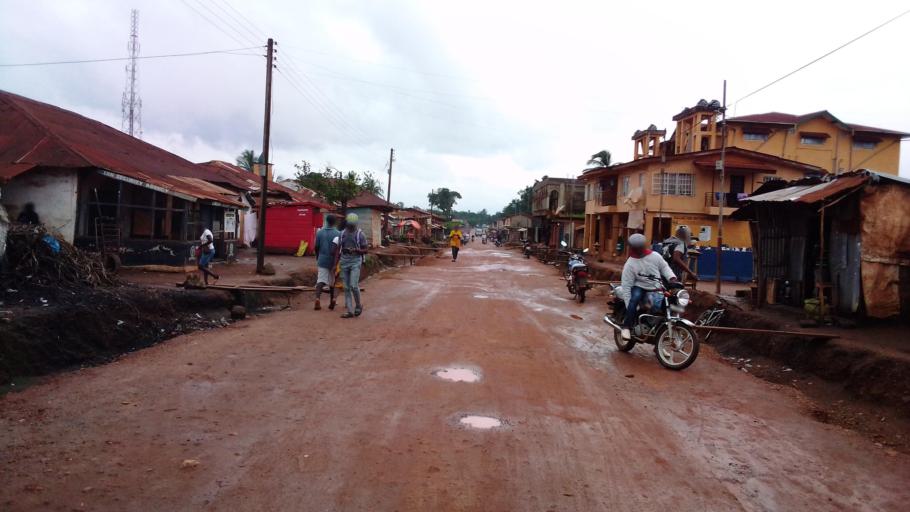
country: SL
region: Eastern Province
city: Kenema
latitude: 7.8719
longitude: -11.1926
